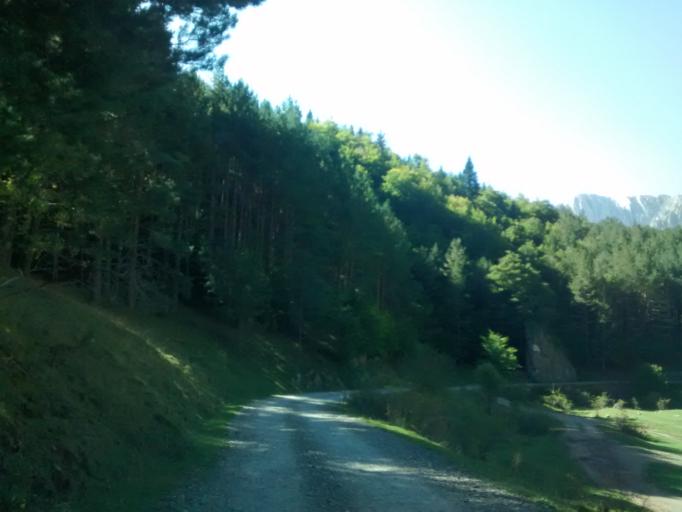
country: ES
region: Aragon
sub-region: Provincia de Huesca
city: Aragues del Puerto
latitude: 42.8499
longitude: -0.7042
